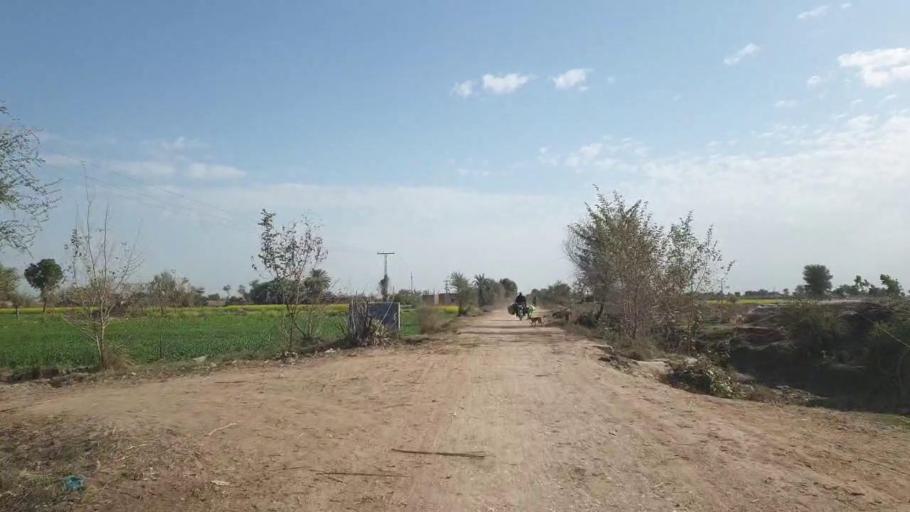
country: PK
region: Sindh
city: Shahdadpur
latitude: 26.0203
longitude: 68.4942
